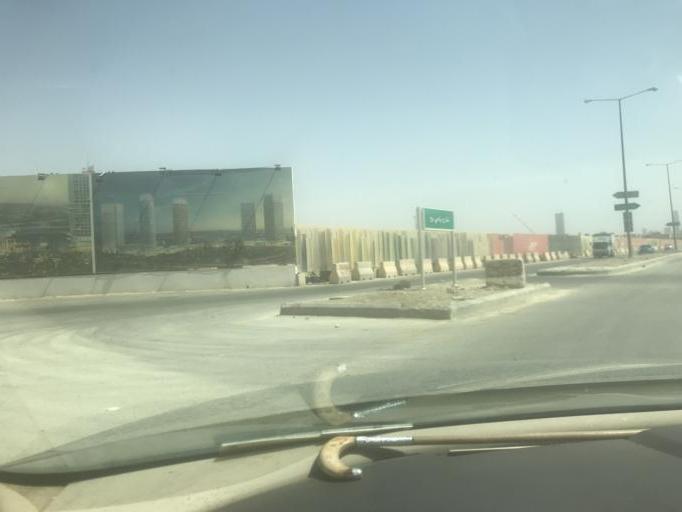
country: SA
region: Ar Riyad
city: Riyadh
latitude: 24.8229
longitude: 46.6061
